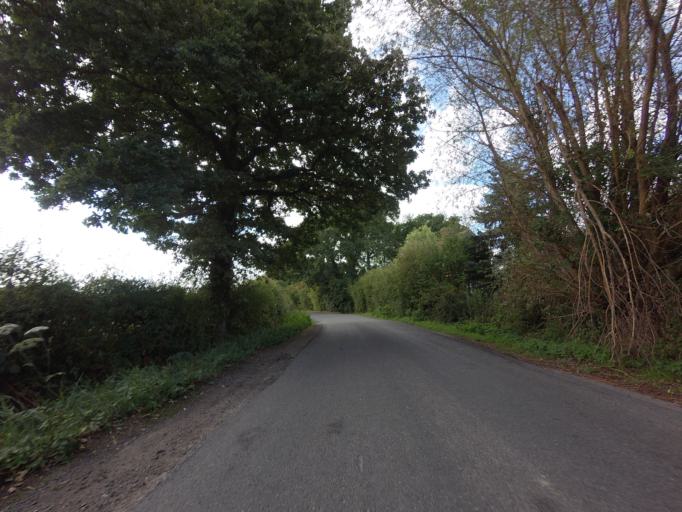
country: GB
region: England
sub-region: Kent
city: Staplehurst
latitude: 51.1530
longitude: 0.5208
